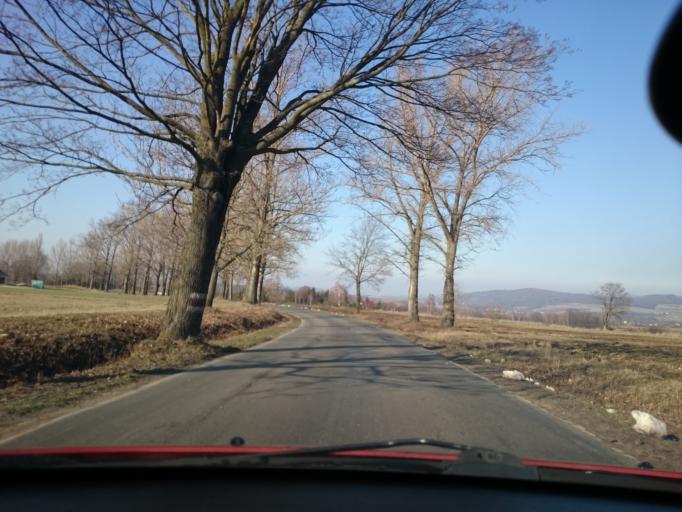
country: PL
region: Lower Silesian Voivodeship
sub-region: Powiat klodzki
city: Bystrzyca Klodzka
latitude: 50.3187
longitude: 16.6138
